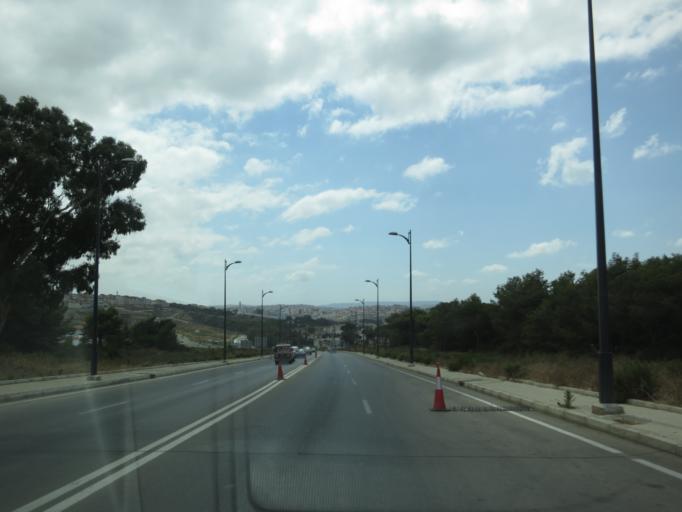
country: MA
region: Tanger-Tetouan
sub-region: Tanger-Assilah
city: Tangier
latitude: 35.7910
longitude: -5.7529
